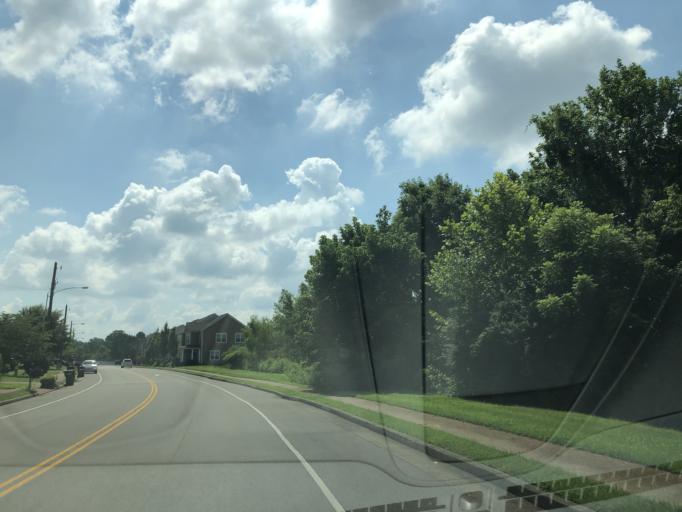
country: US
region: Tennessee
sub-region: Williamson County
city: Nolensville
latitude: 36.0122
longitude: -86.6968
